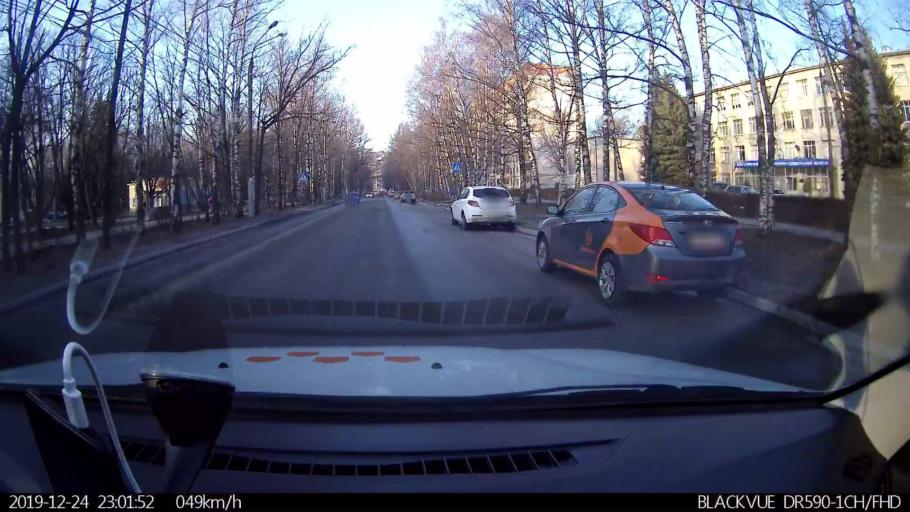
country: RU
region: Nizjnij Novgorod
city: Nizhniy Novgorod
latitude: 56.2689
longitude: 43.9236
